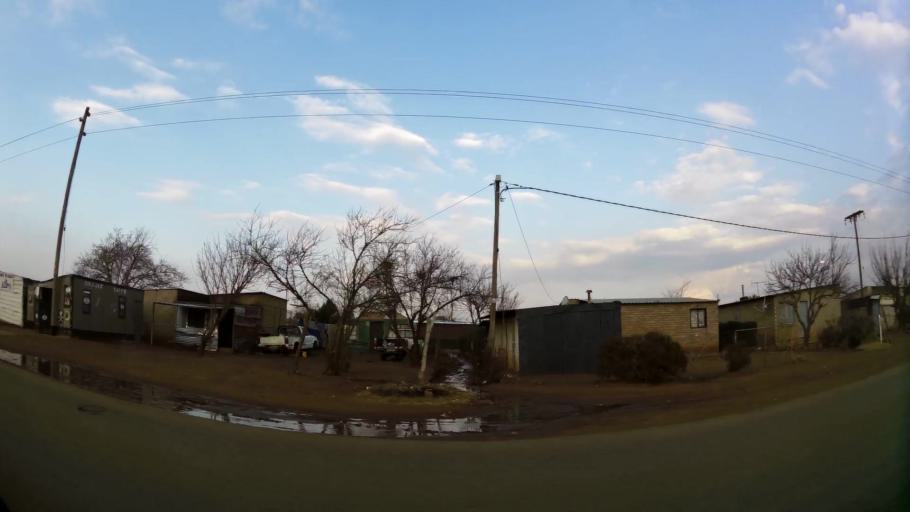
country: ZA
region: Gauteng
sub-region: City of Johannesburg Metropolitan Municipality
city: Orange Farm
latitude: -26.5498
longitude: 27.8329
